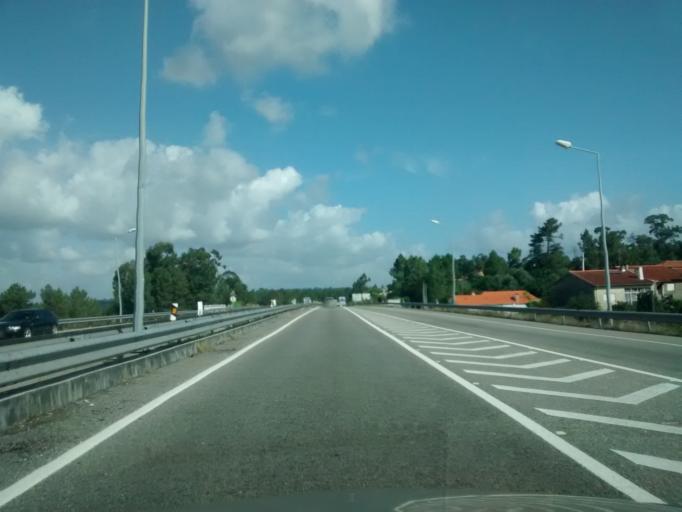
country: PT
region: Aveiro
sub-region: Oliveira do Bairro
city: Oliveira do Bairro
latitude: 40.5149
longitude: -8.5008
